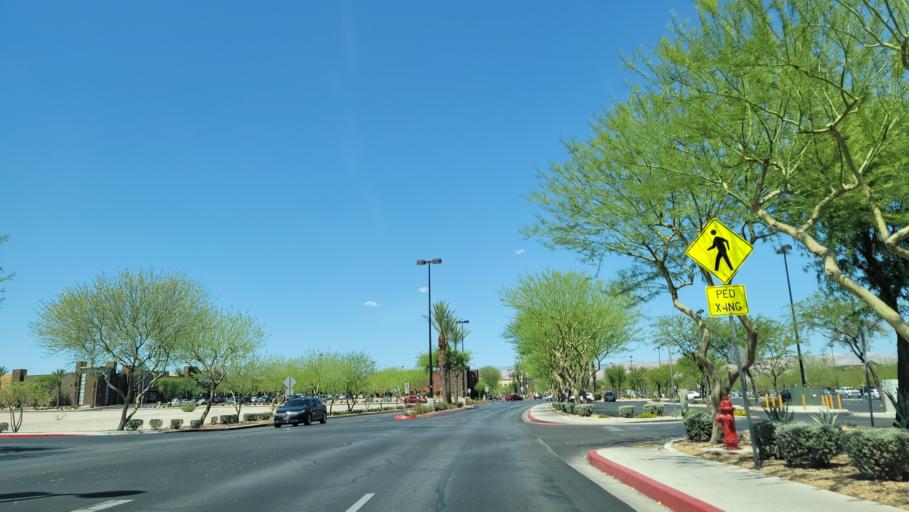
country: US
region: Nevada
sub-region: Clark County
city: Enterprise
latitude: 36.0634
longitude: -115.2455
